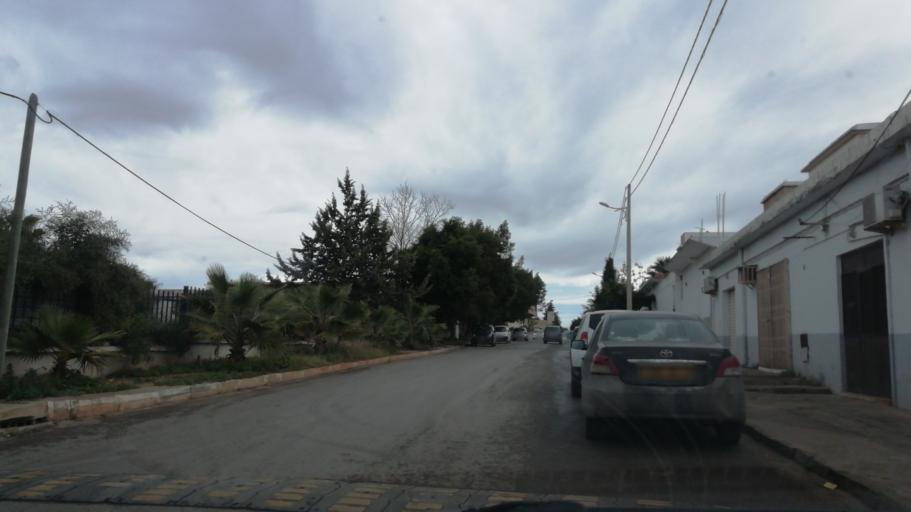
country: DZ
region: Oran
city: Oran
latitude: 35.6952
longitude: -0.6026
